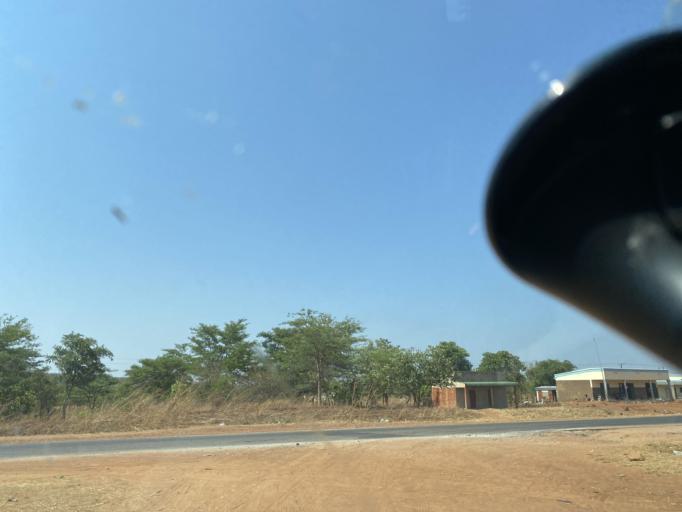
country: ZM
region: Lusaka
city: Chongwe
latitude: -15.2906
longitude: 28.8150
